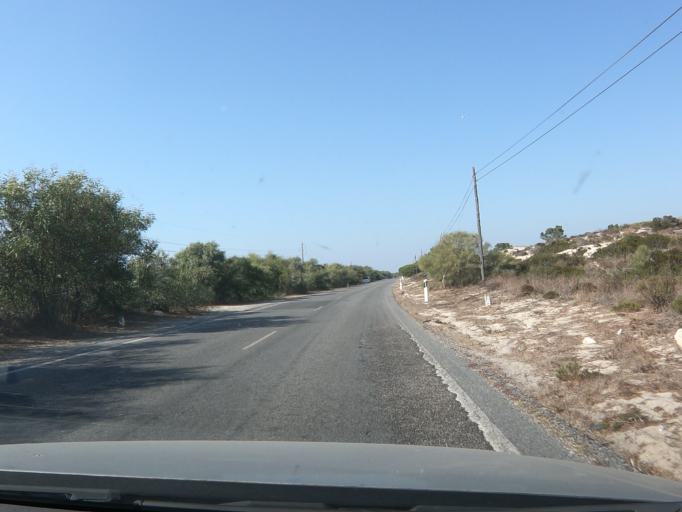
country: PT
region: Setubal
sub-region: Setubal
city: Setubal
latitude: 38.3967
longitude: -8.8050
